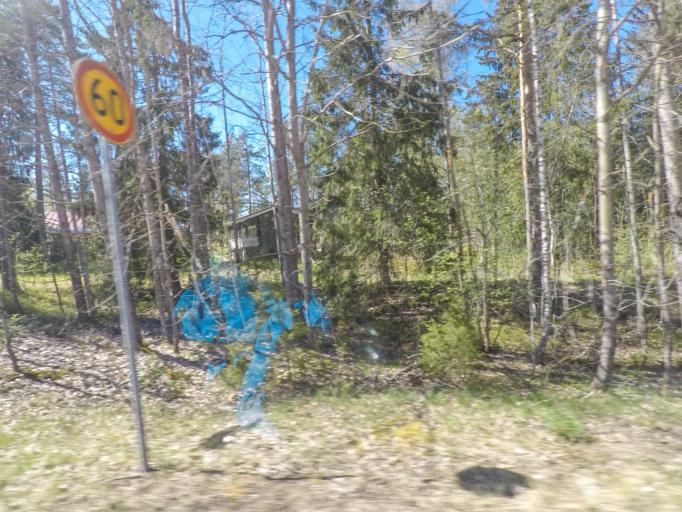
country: FI
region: Uusimaa
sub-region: Helsinki
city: Sammatti
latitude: 60.3539
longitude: 23.8011
